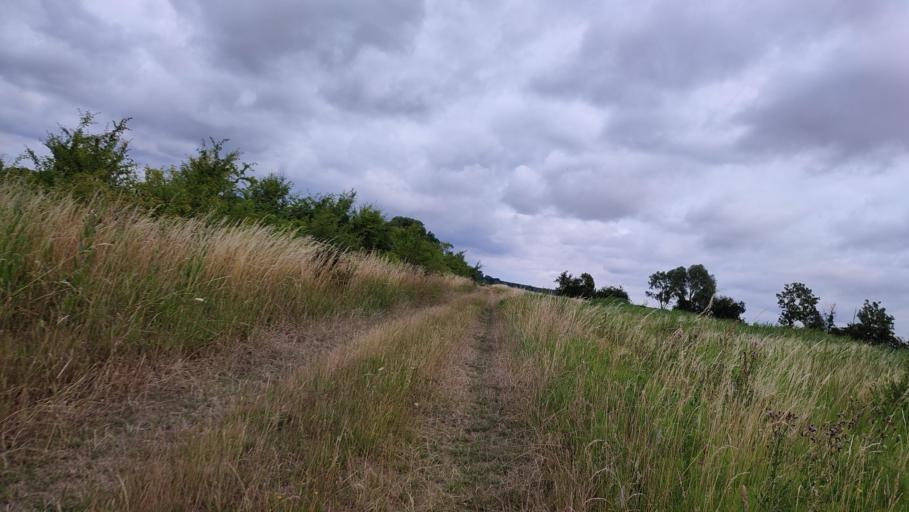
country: DE
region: Lower Saxony
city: Hitzacker
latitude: 53.1644
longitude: 11.1033
